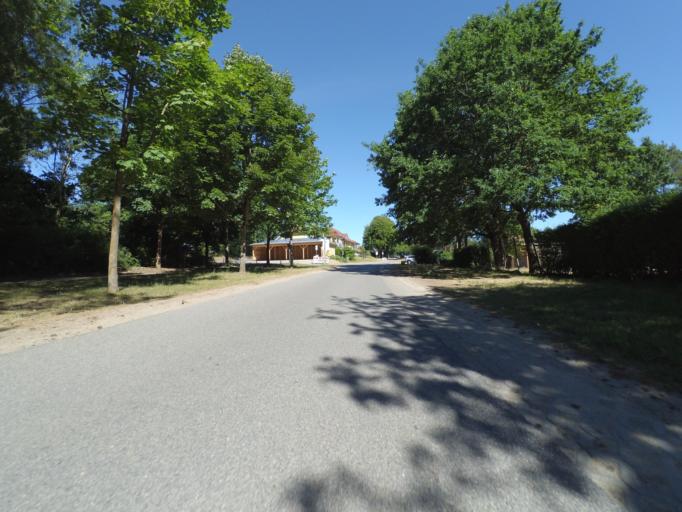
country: DE
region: Mecklenburg-Vorpommern
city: Plau am See
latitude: 53.4881
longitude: 12.2801
